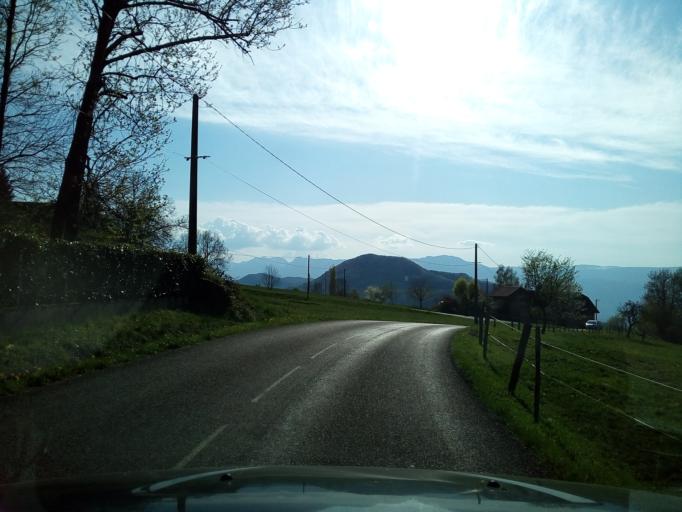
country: FR
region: Rhone-Alpes
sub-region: Departement de l'Isere
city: Revel
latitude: 45.1871
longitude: 5.8826
